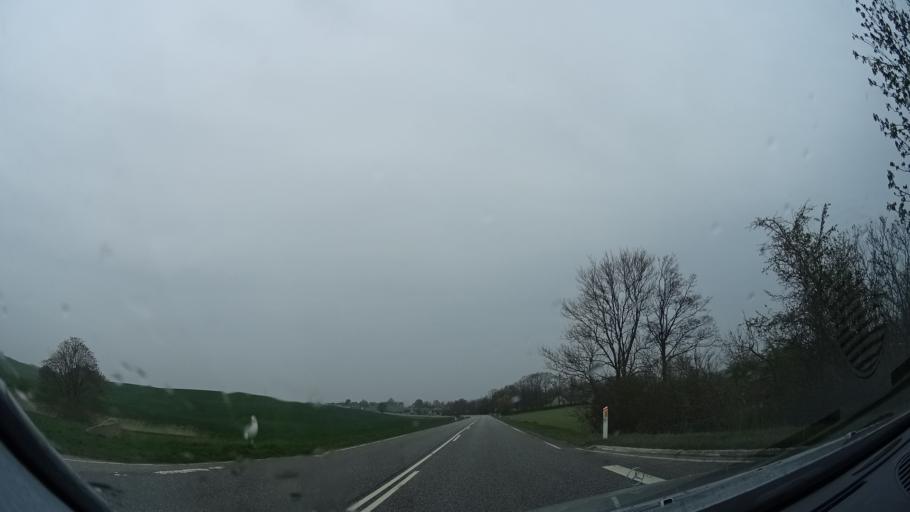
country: DK
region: Zealand
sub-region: Odsherred Kommune
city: Asnaes
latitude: 55.7956
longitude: 11.6022
